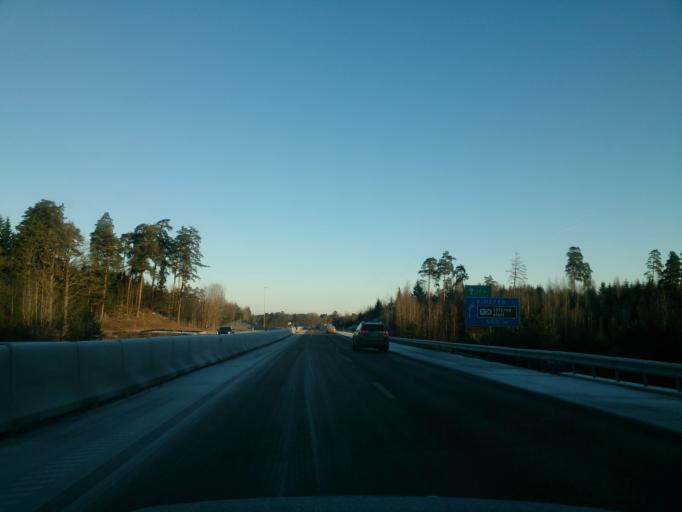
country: SE
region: OEstergoetland
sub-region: Norrkopings Kommun
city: Kimstad
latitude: 58.5467
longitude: 16.0468
